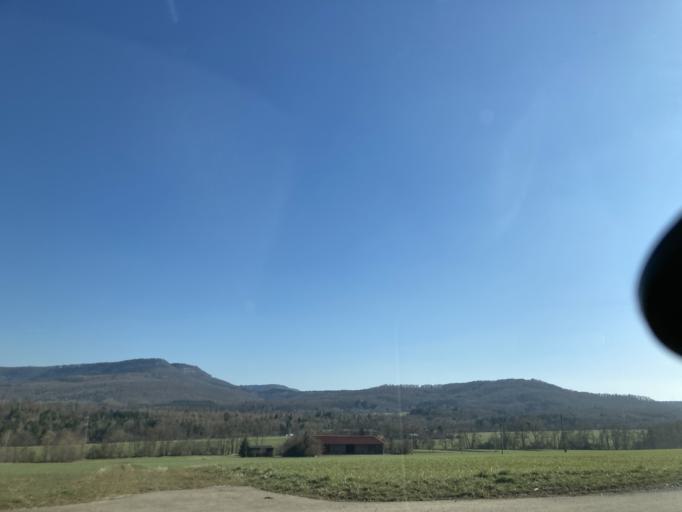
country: DE
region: Baden-Wuerttemberg
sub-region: Tuebingen Region
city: Ofterdingen
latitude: 48.3990
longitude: 9.0122
